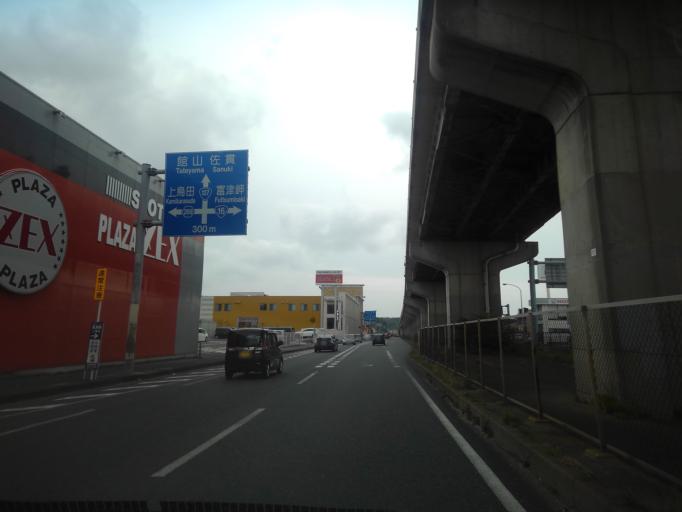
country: JP
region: Chiba
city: Kisarazu
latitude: 35.3698
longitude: 139.9295
